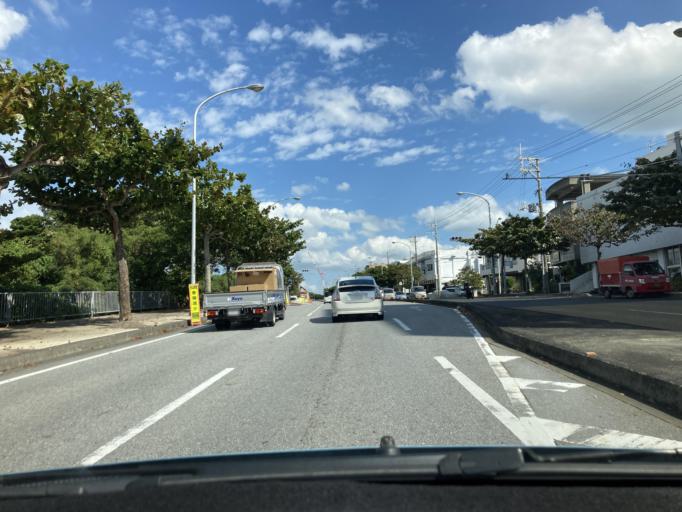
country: JP
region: Okinawa
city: Ginowan
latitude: 26.2866
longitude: 127.7599
